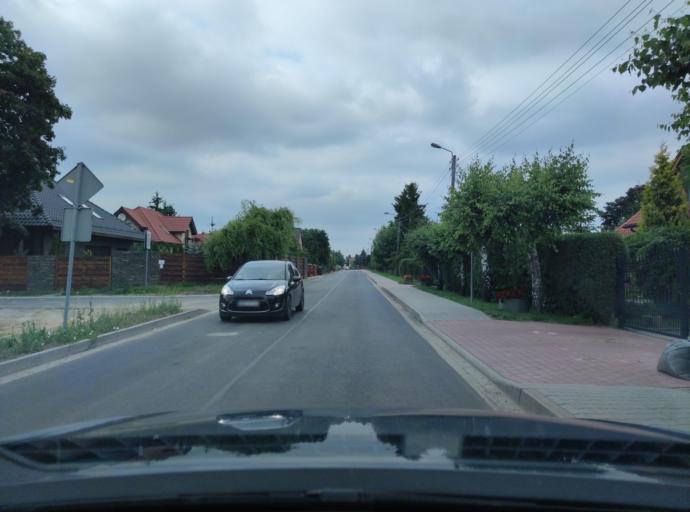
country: PL
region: Lower Silesian Voivodeship
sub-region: Powiat wroclawski
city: Tyniec Maly
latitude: 51.0012
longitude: 16.9062
